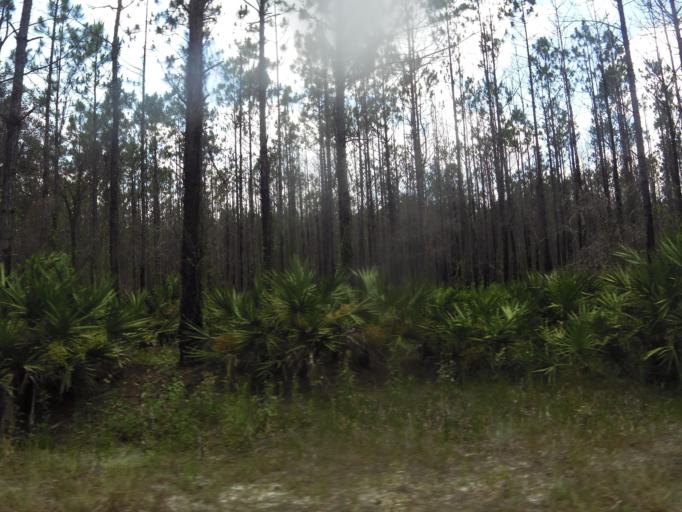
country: US
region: Florida
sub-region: Clay County
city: Keystone Heights
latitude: 29.8565
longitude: -81.8537
